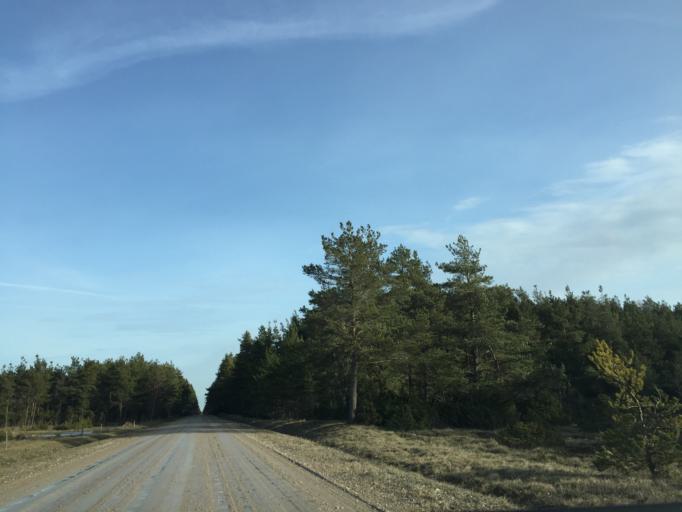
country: EE
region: Saare
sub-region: Kuressaare linn
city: Kuressaare
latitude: 58.2857
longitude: 21.9271
